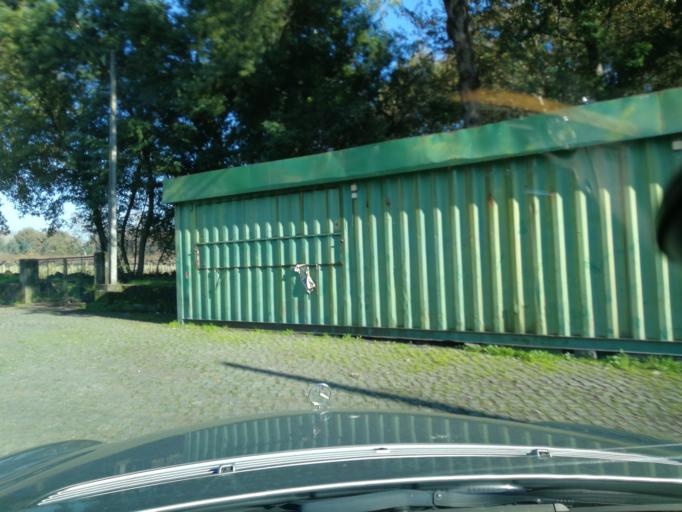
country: PT
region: Braga
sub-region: Braga
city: Adaufe
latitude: 41.6074
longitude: -8.4009
